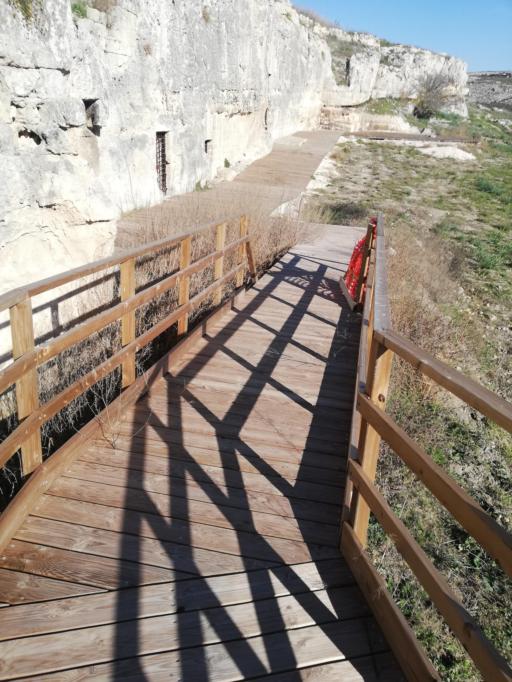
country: IT
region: Apulia
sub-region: Provincia di Bari
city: Gravina in Puglia
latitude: 40.8284
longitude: 16.3984
